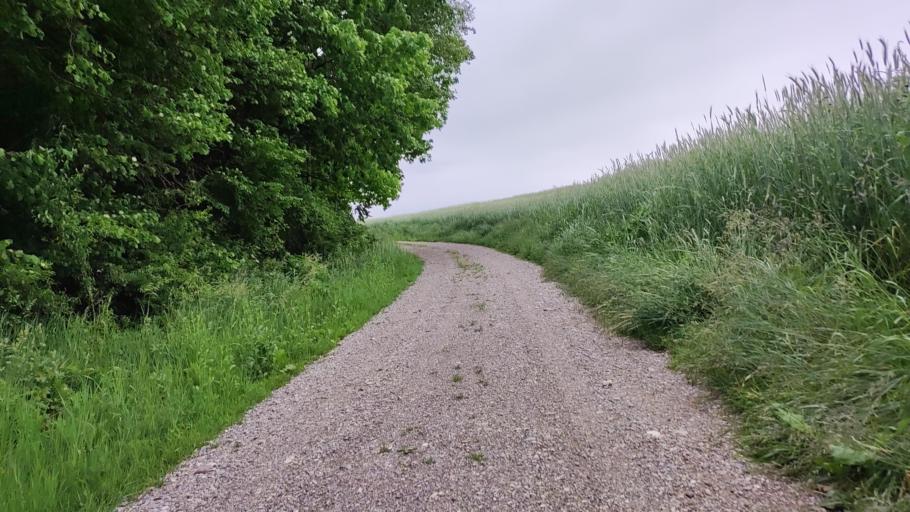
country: DE
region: Bavaria
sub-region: Swabia
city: Dinkelscherben
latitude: 48.3525
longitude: 10.5502
